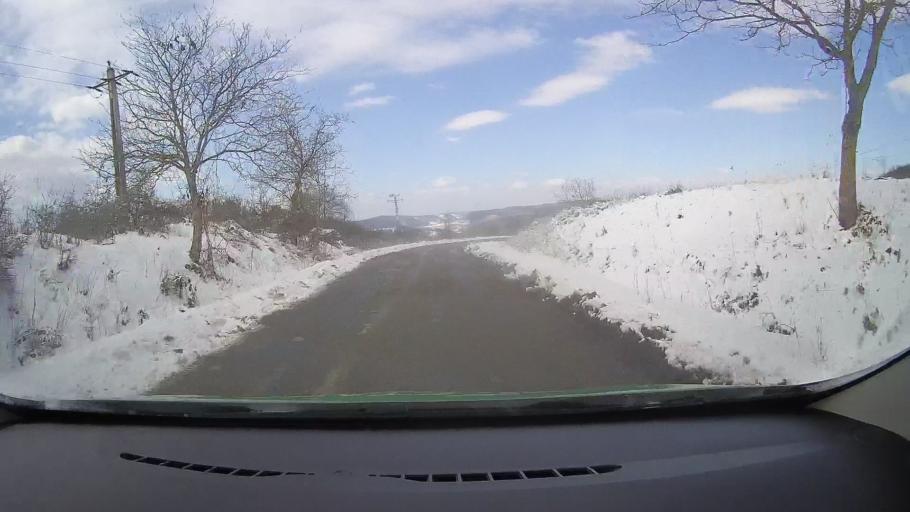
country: RO
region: Sibiu
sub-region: Comuna Mihaileni
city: Mihaileni
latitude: 46.0023
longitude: 24.4264
